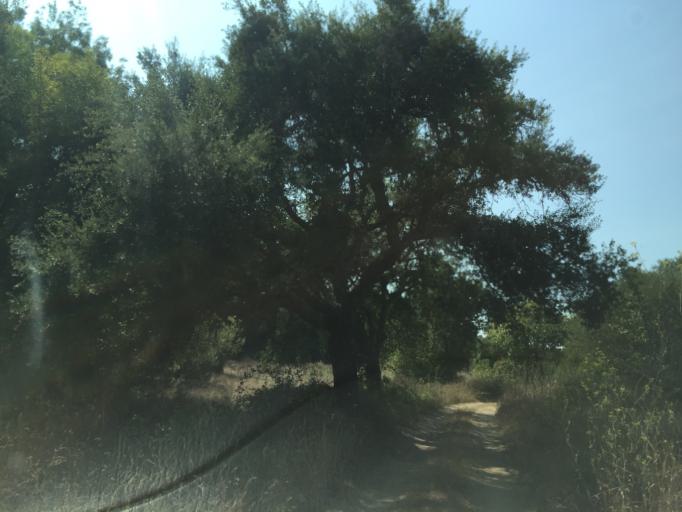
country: PT
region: Setubal
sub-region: Santiago do Cacem
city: Santiago do Cacem
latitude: 37.9712
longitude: -8.5125
